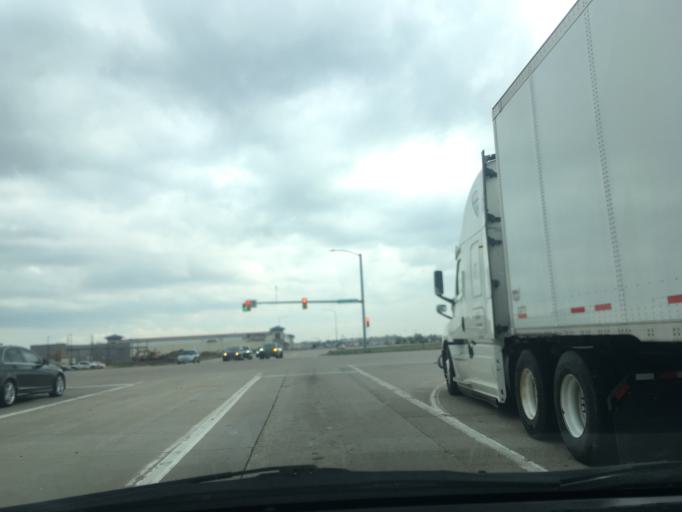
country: US
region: Colorado
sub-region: Weld County
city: Firestone
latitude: 40.1610
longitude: -104.9755
